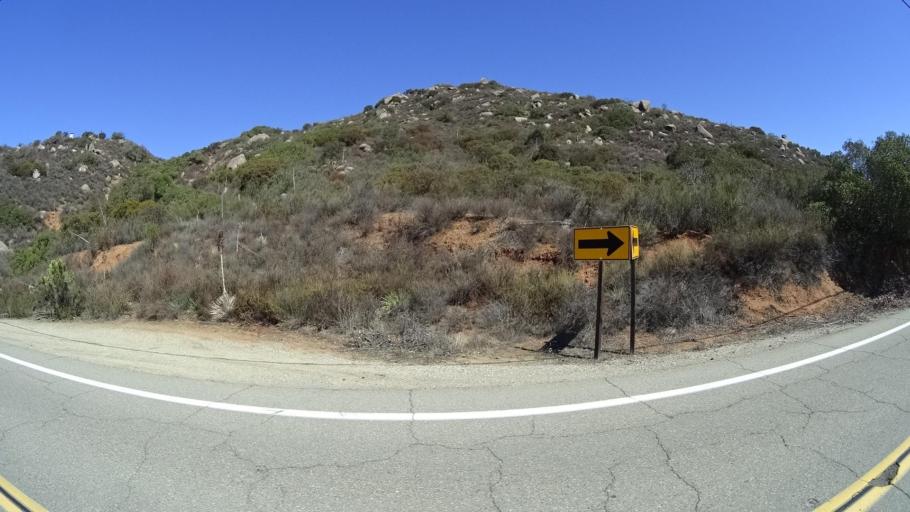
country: US
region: California
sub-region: San Diego County
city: Alpine
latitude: 32.8022
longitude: -116.7647
